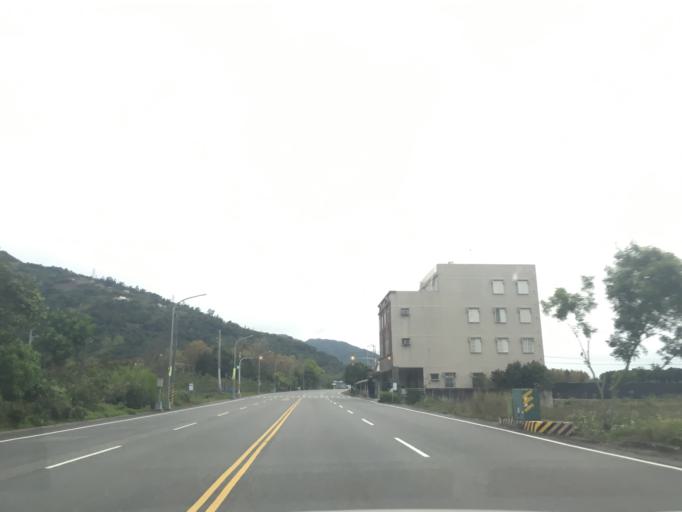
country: TW
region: Taiwan
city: Taitung City
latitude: 22.7293
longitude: 121.0562
